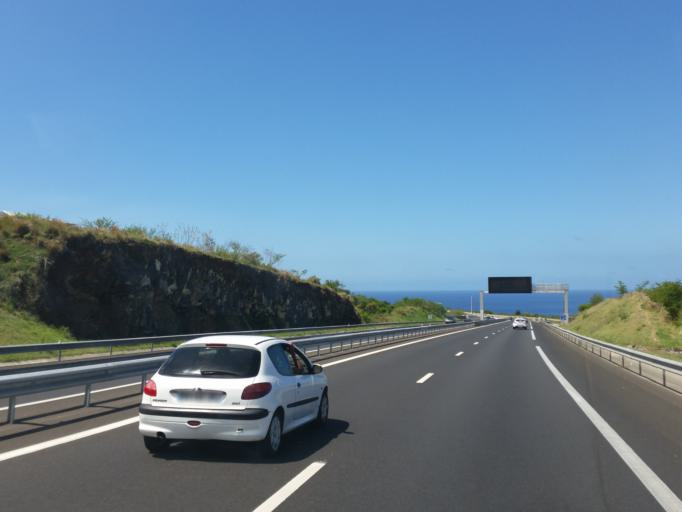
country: RE
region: Reunion
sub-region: Reunion
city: Saint-Leu
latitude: -21.1977
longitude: 55.2954
